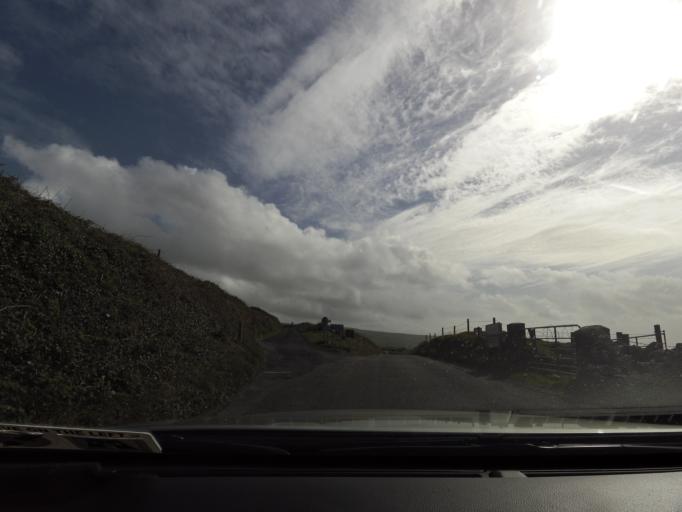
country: IE
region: Connaught
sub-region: County Galway
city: Bearna
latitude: 53.1089
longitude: -9.2930
